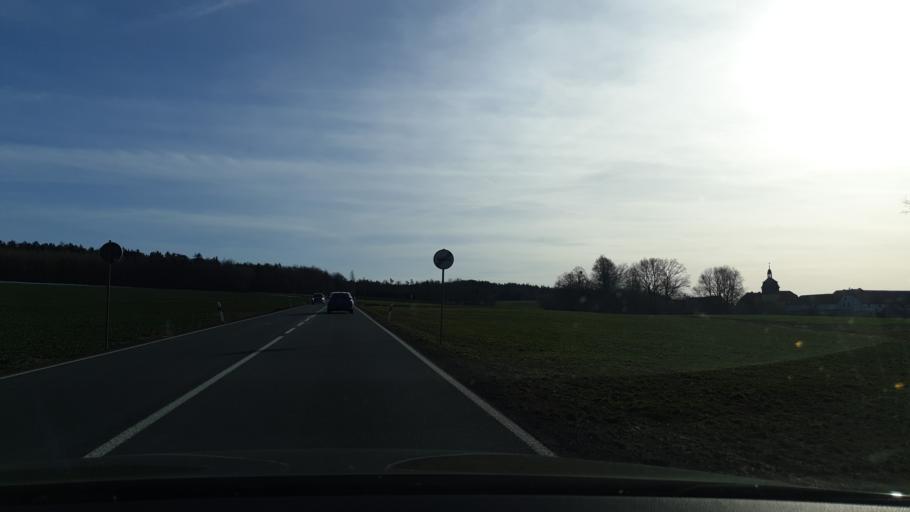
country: DE
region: Thuringia
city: Teichwitz
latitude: 50.7608
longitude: 12.0895
